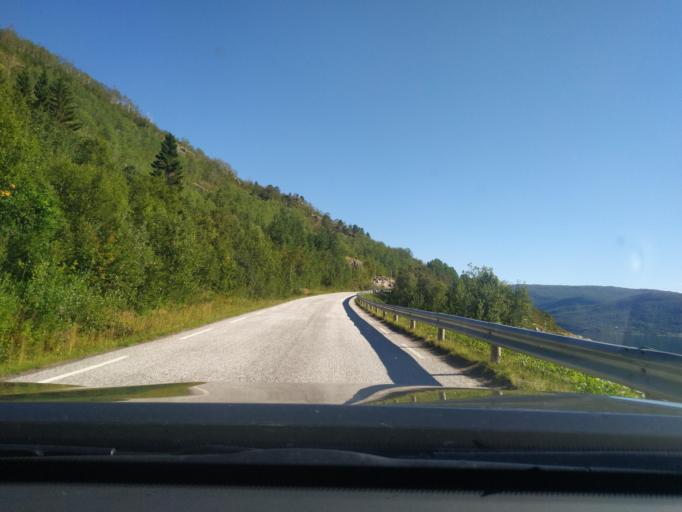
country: NO
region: Troms
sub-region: Dyroy
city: Brostadbotn
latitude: 68.9218
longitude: 17.6258
